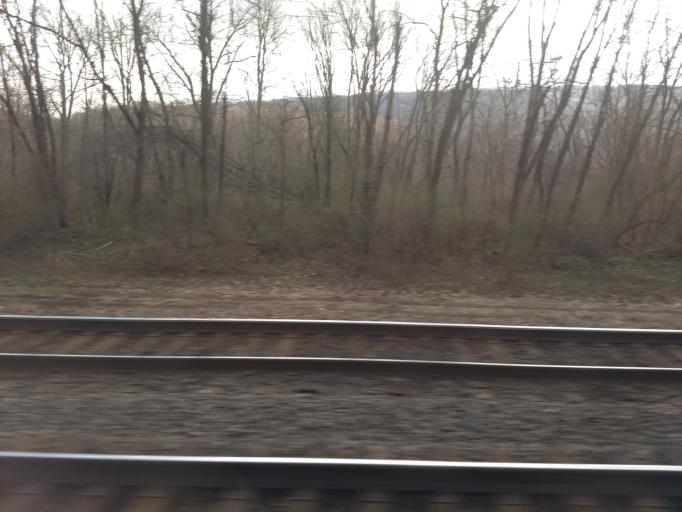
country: US
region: Pennsylvania
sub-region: Blair County
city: Bellwood
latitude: 40.6152
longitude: -78.3221
